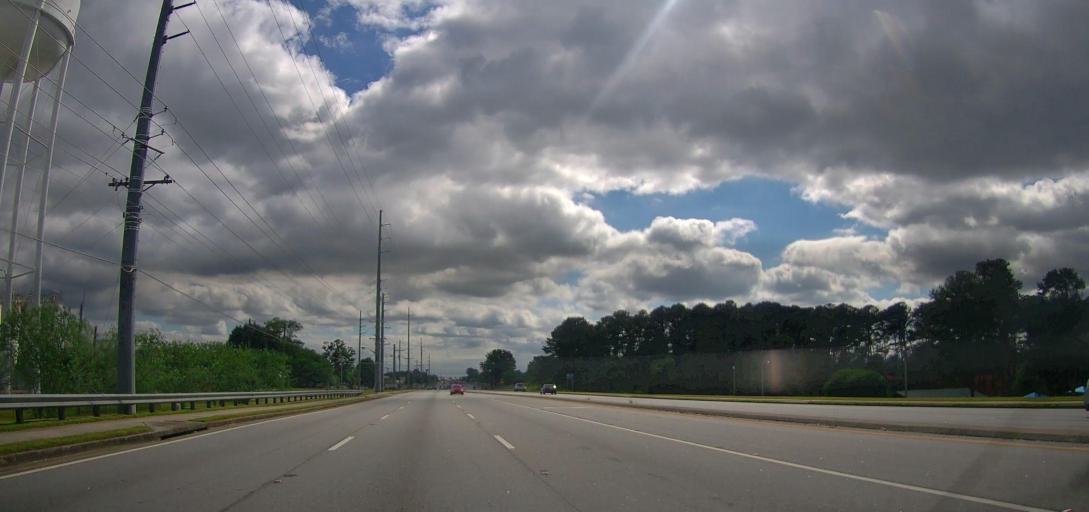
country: US
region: Georgia
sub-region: Rockdale County
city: Conyers
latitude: 33.6618
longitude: -83.9966
